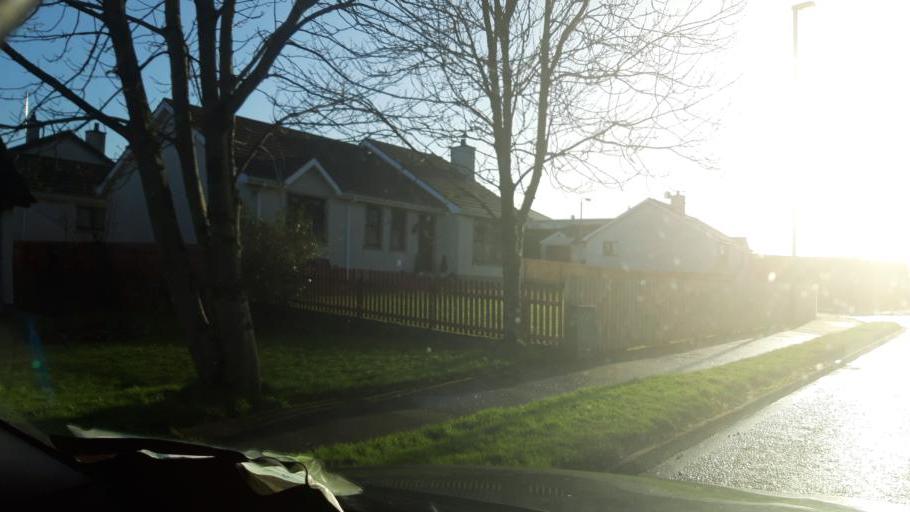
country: GB
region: Northern Ireland
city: Garvagh
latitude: 54.9783
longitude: -6.6893
